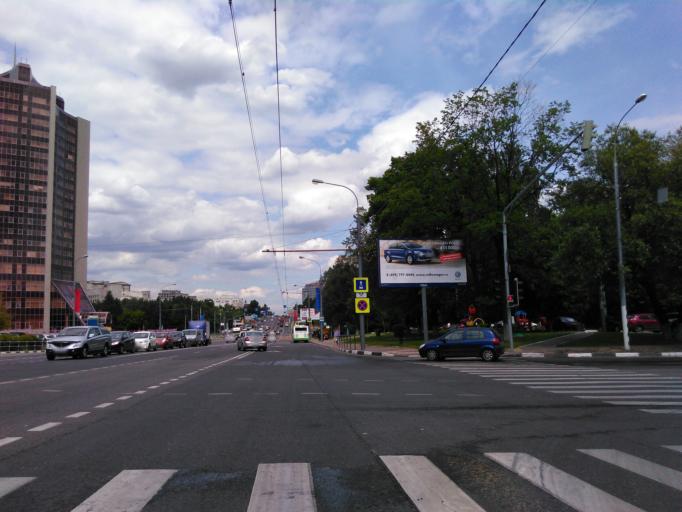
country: RU
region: Moscow
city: Zyuzino
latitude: 55.6638
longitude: 37.5789
